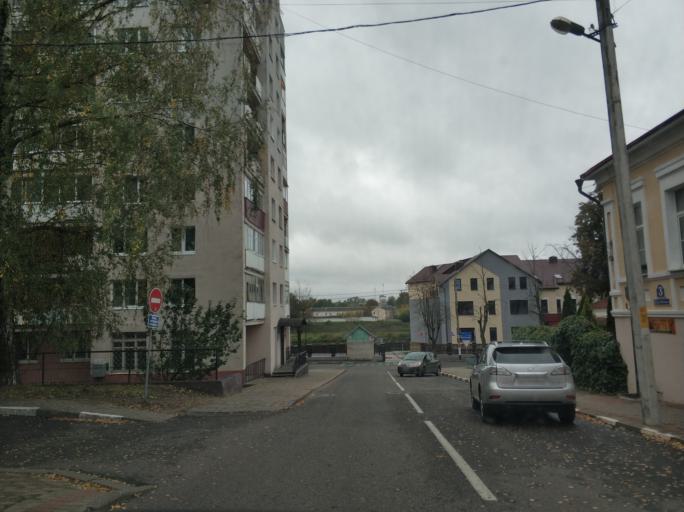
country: BY
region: Vitebsk
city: Polatsk
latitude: 55.4844
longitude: 28.7722
